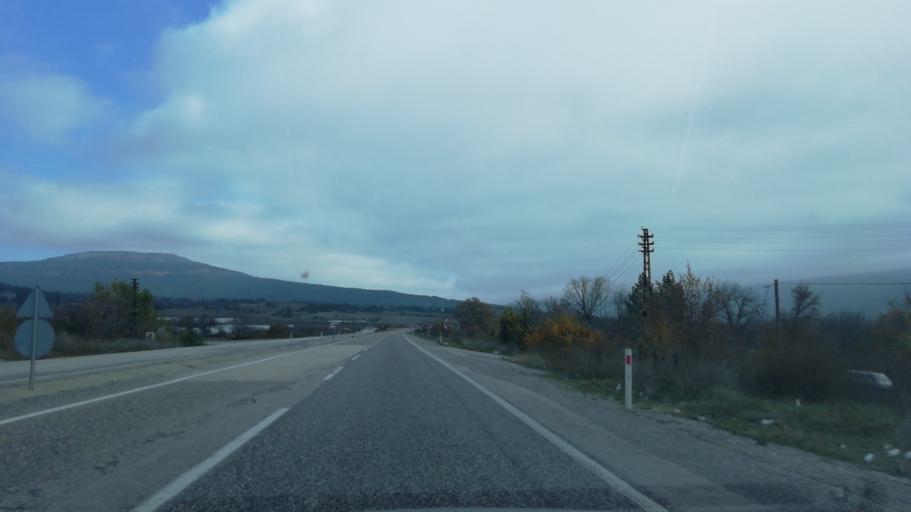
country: TR
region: Karabuk
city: Safranbolu
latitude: 41.2235
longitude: 32.7755
